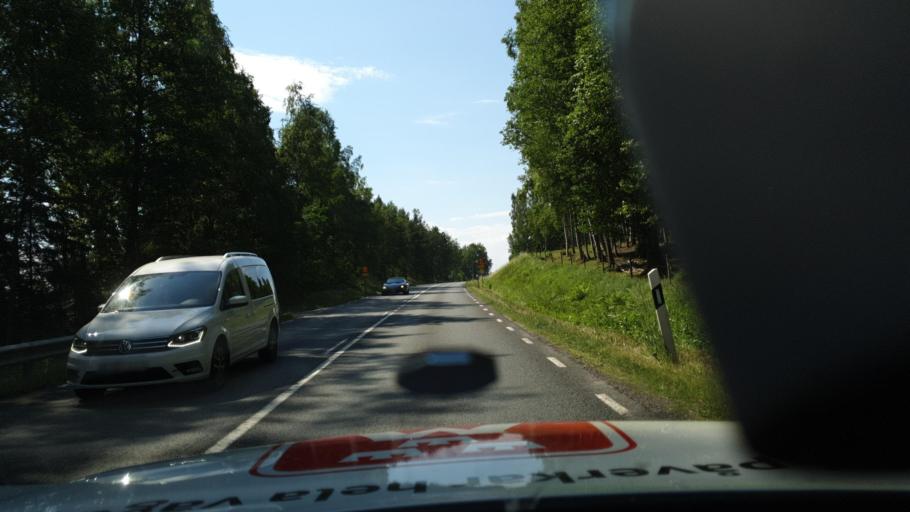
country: SE
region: Vaestra Goetaland
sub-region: Hjo Kommun
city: Hjo
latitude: 58.1004
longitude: 14.2076
